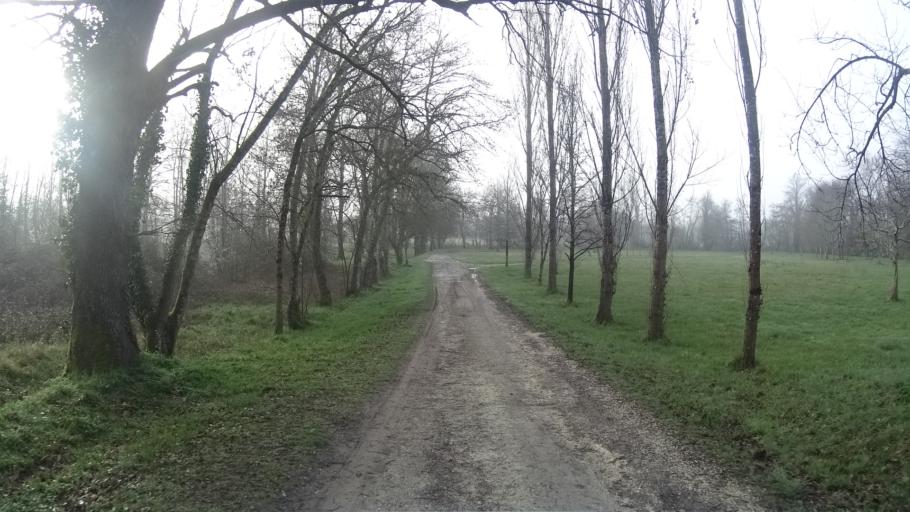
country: FR
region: Poitou-Charentes
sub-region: Departement de la Charente-Maritime
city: Saint-Aigulin
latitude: 45.1496
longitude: -0.0138
